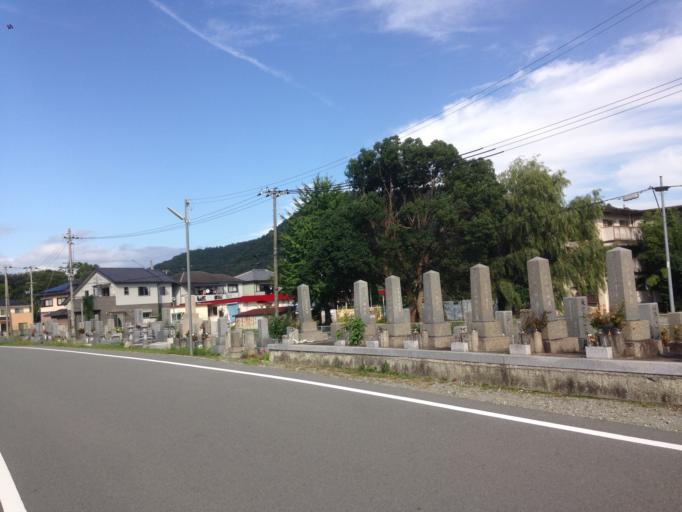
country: JP
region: Hyogo
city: Tatsunocho-tominaga
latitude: 34.8670
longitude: 134.5507
